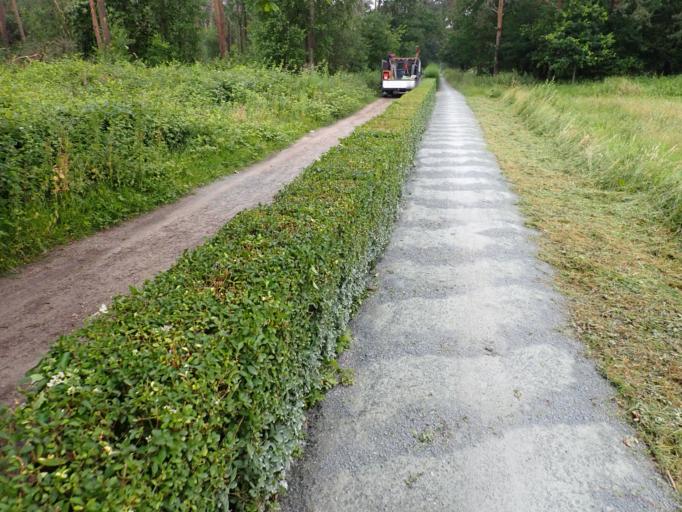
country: BE
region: Flanders
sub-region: Provincie Antwerpen
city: Hoboken
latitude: 51.1569
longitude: 4.3567
